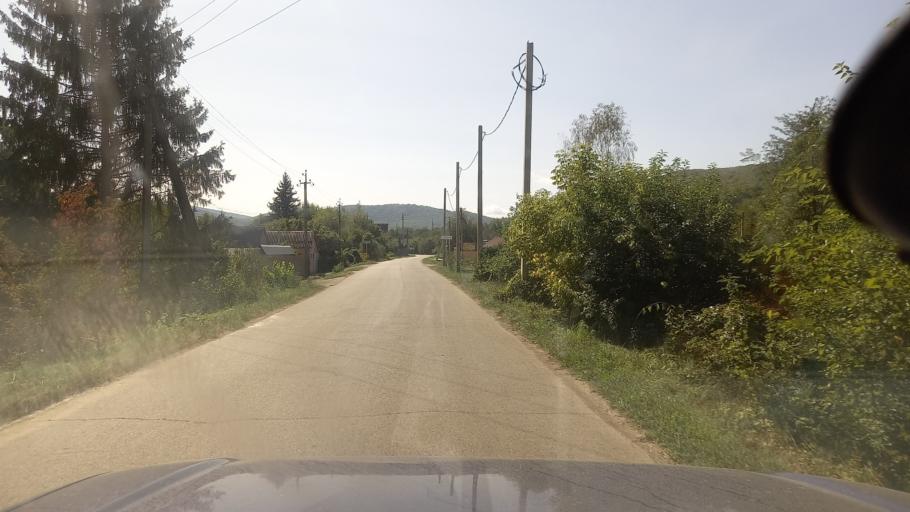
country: RU
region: Krasnodarskiy
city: Azovskaya
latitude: 44.7081
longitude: 38.6729
